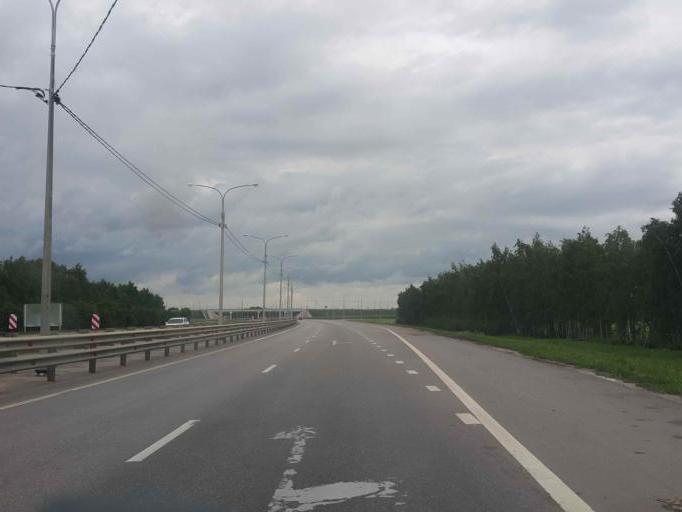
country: RU
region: Tambov
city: Zavoronezhskoye
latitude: 52.8569
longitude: 40.7750
